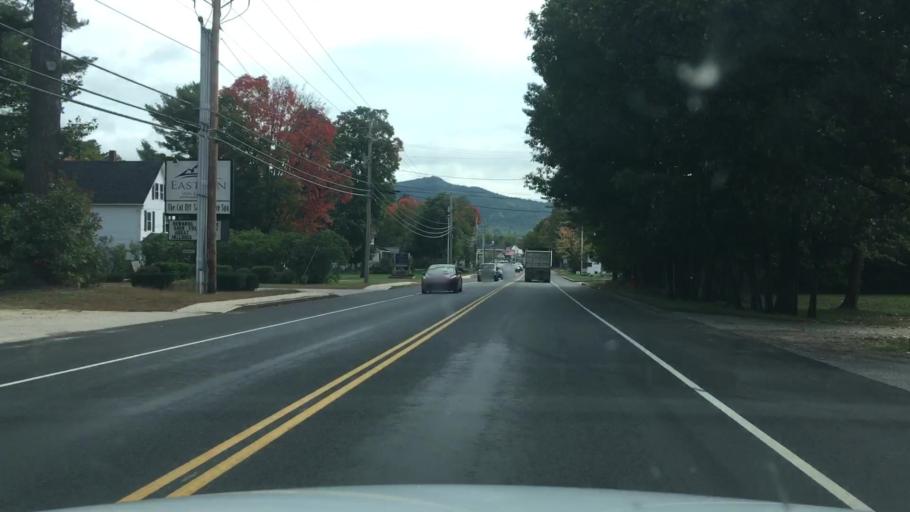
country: US
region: New Hampshire
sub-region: Carroll County
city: North Conway
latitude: 44.0585
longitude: -71.1354
